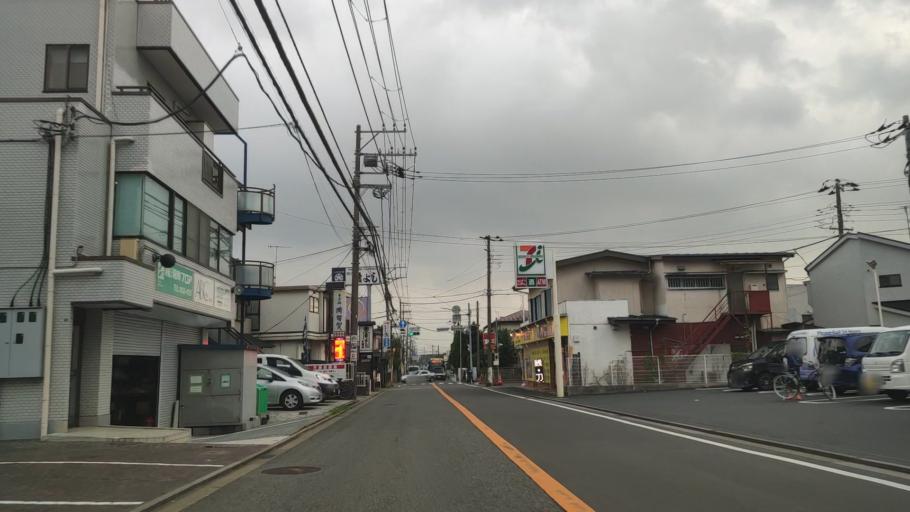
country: JP
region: Kanagawa
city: Minami-rinkan
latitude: 35.4194
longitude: 139.5005
